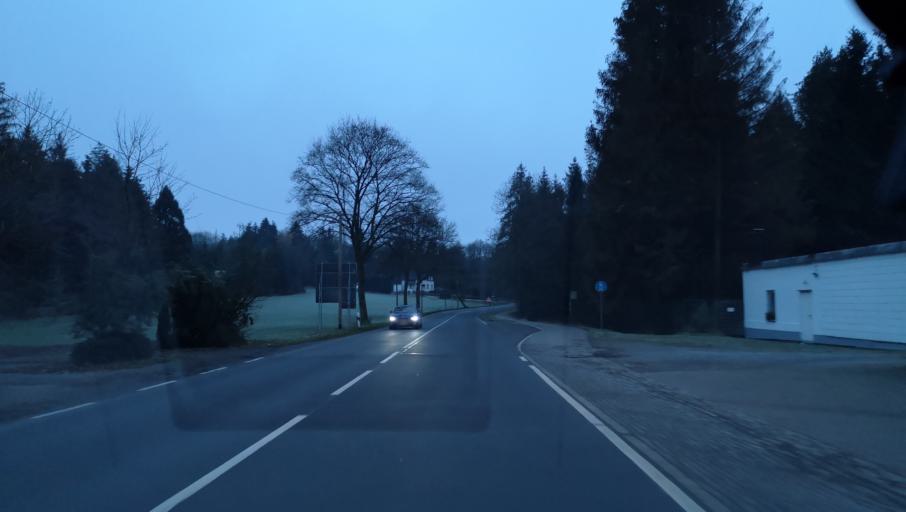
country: DE
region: North Rhine-Westphalia
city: Radevormwald
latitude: 51.2111
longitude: 7.3889
